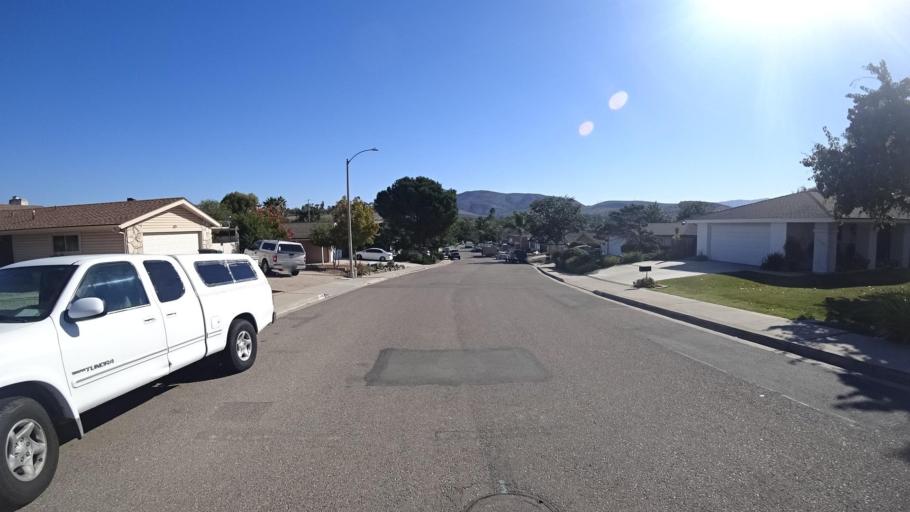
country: US
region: California
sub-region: San Diego County
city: Bonita
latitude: 32.6775
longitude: -117.0099
